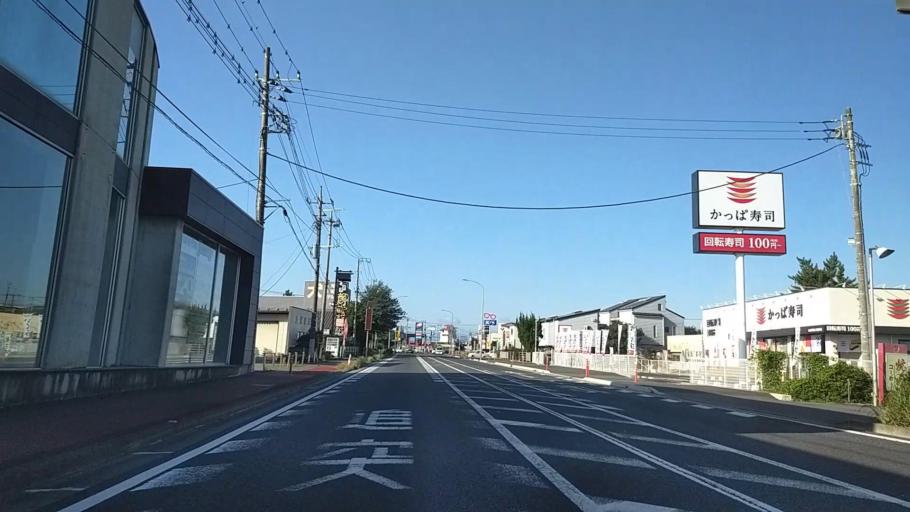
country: JP
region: Gunma
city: Annaka
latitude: 36.3227
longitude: 138.8812
